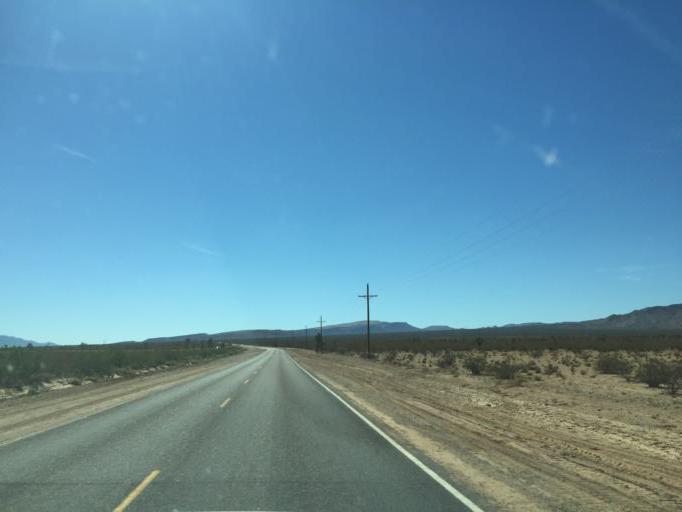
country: US
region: Arizona
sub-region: Mohave County
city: Meadview
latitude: 35.7800
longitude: -114.1306
